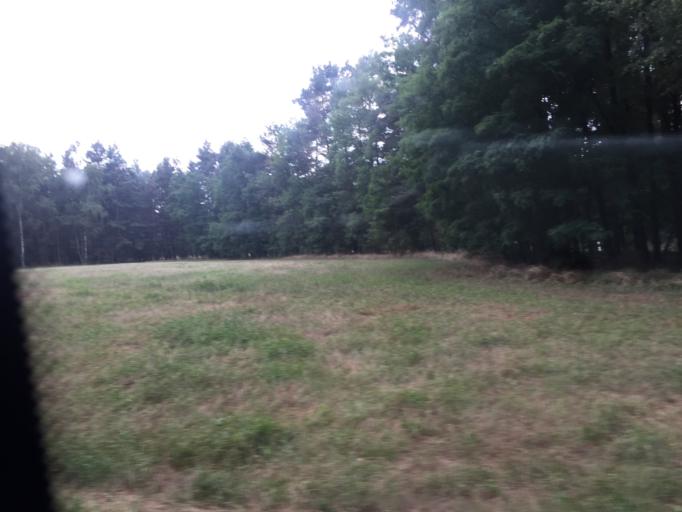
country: DE
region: Saxony
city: Schleife
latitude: 51.5151
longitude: 14.5231
